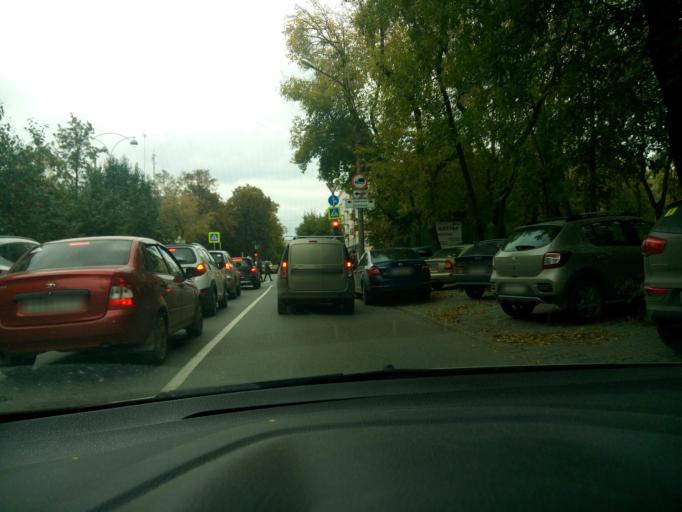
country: RU
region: Sverdlovsk
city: Yekaterinburg
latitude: 56.8403
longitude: 60.6262
